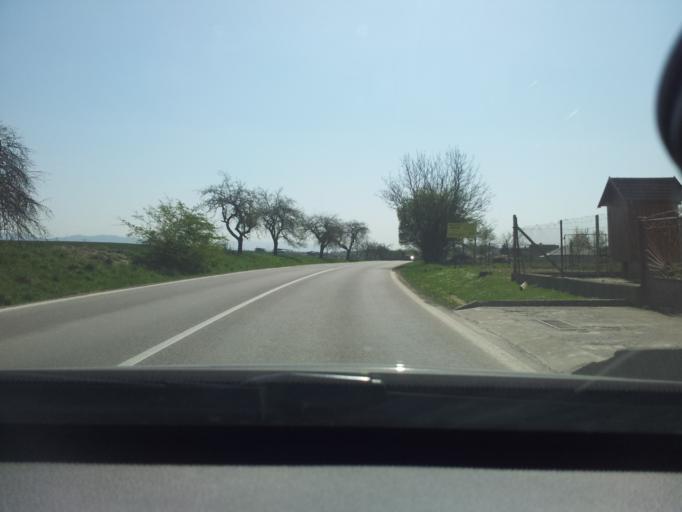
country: SK
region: Nitriansky
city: Banovce nad Bebravou
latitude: 48.7910
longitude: 18.1625
